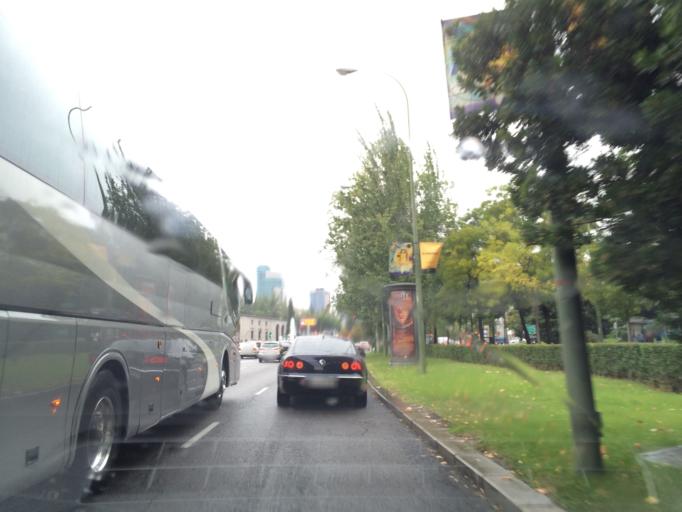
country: ES
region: Madrid
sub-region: Provincia de Madrid
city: Chamberi
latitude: 40.4399
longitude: -3.6912
